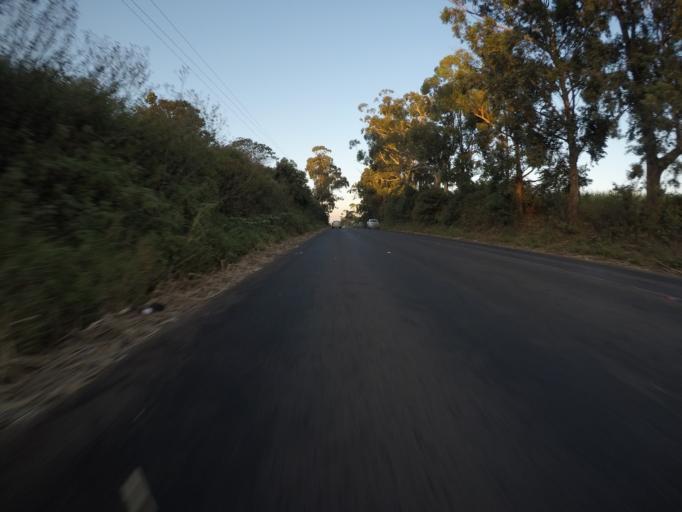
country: ZA
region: KwaZulu-Natal
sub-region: uThungulu District Municipality
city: Empangeni
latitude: -28.7993
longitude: 31.8951
